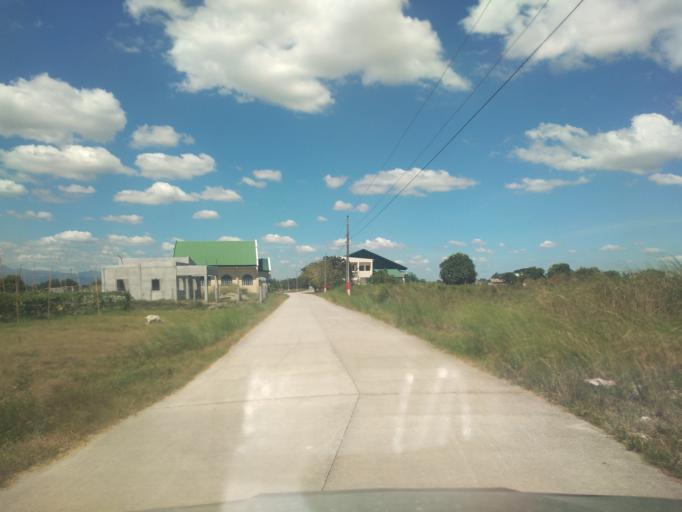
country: PH
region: Central Luzon
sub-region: Province of Pampanga
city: San Basilio
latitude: 15.0342
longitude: 120.6053
